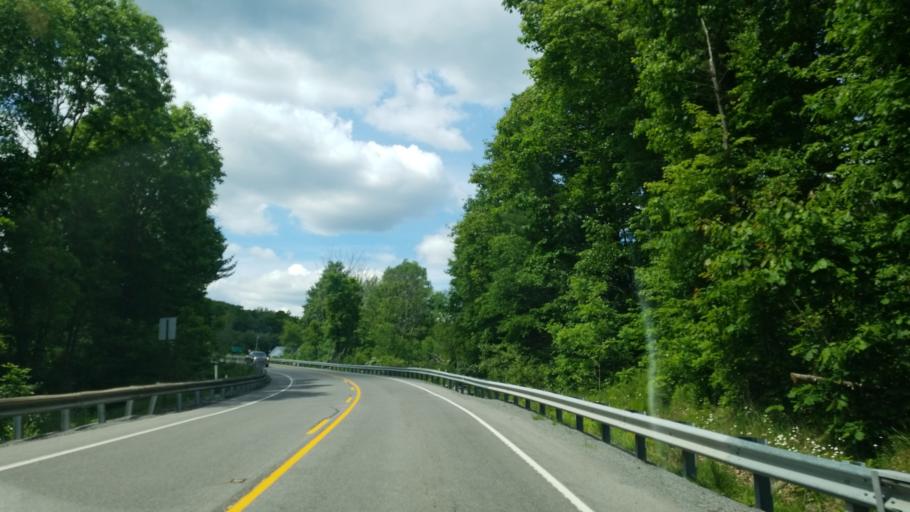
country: US
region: Pennsylvania
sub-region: Clearfield County
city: Clearfield
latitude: 40.9644
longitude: -78.3691
